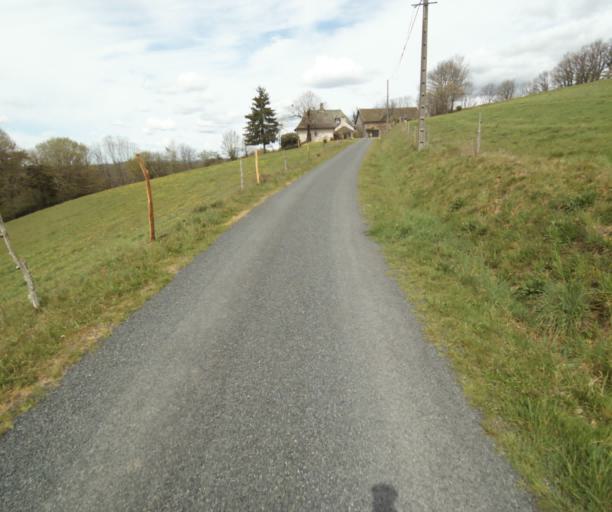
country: FR
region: Limousin
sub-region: Departement de la Correze
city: Sainte-Fortunade
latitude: 45.2039
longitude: 1.8535
